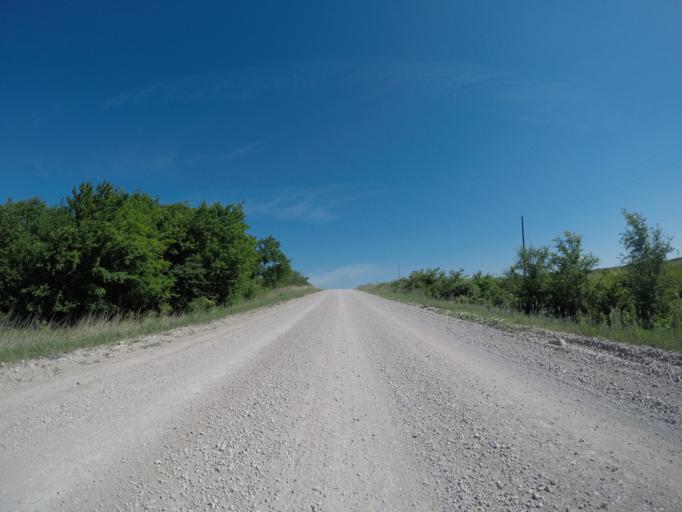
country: US
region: Kansas
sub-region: Wabaunsee County
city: Alma
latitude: 38.9735
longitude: -96.1140
